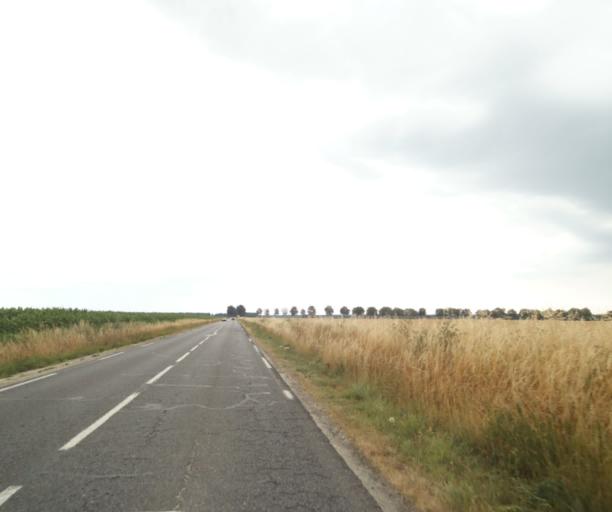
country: FR
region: Ile-de-France
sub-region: Departement de Seine-et-Marne
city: Perthes
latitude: 48.4909
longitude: 2.5783
